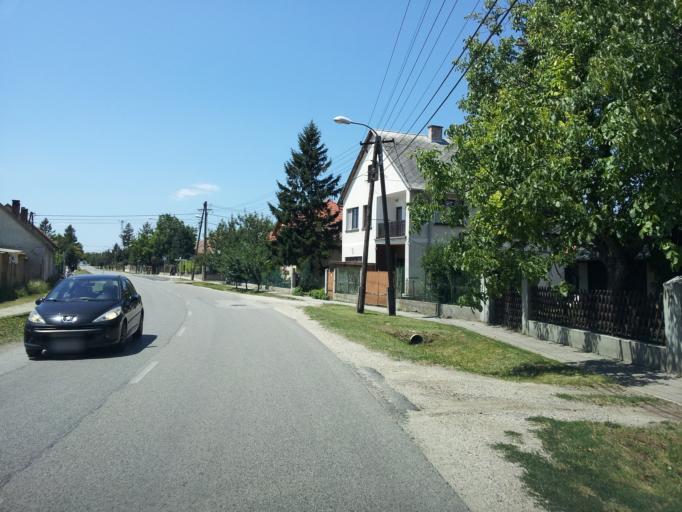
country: HU
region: Veszprem
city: Berhida
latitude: 47.1142
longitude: 18.1241
